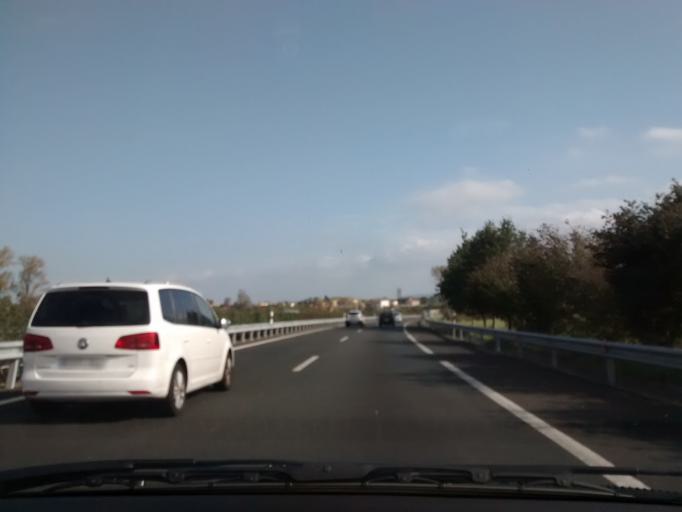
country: ES
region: Cantabria
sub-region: Provincia de Cantabria
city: El Astillero
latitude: 43.4005
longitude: -3.7750
